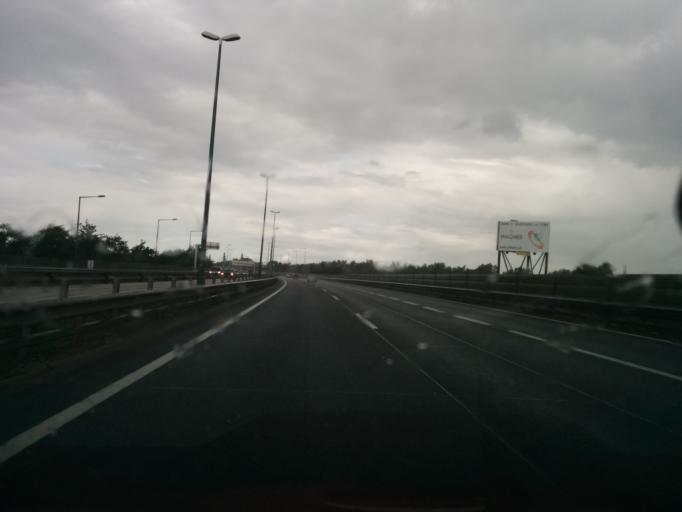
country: AT
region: Lower Austria
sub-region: Politischer Bezirk Wien-Umgebung
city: Schwechat
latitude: 48.1758
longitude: 16.4545
